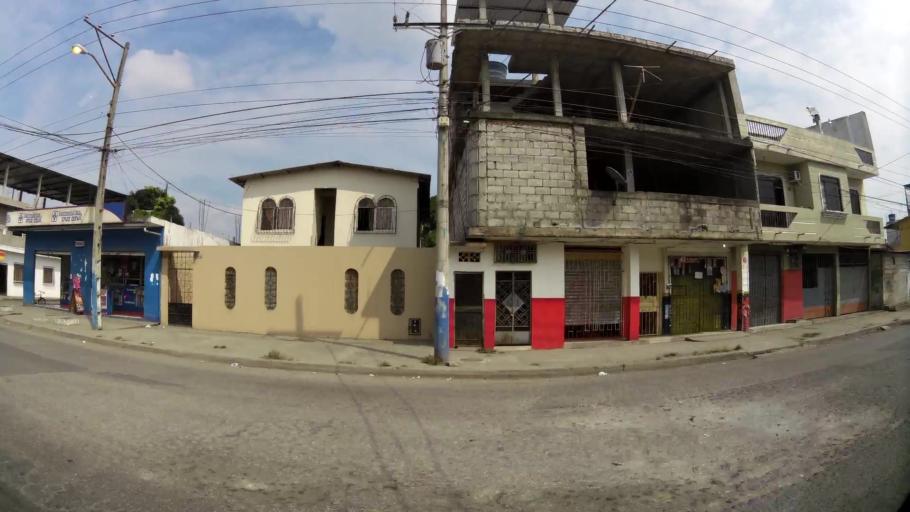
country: EC
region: Guayas
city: Guayaquil
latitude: -2.2411
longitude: -79.9068
